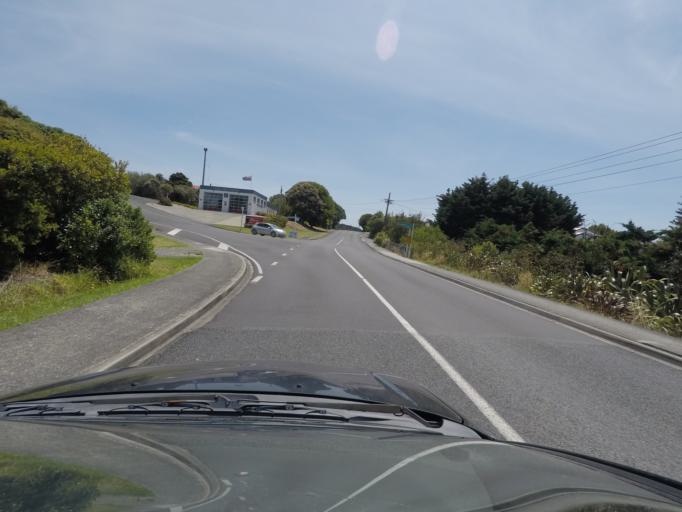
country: NZ
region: Auckland
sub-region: Auckland
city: Warkworth
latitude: -36.2926
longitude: 174.8035
